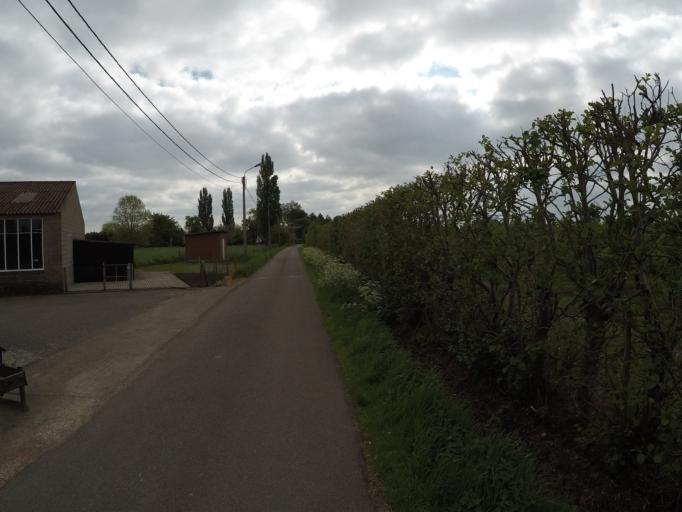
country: BE
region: Flanders
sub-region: Provincie Antwerpen
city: Ranst
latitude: 51.1766
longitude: 4.5450
